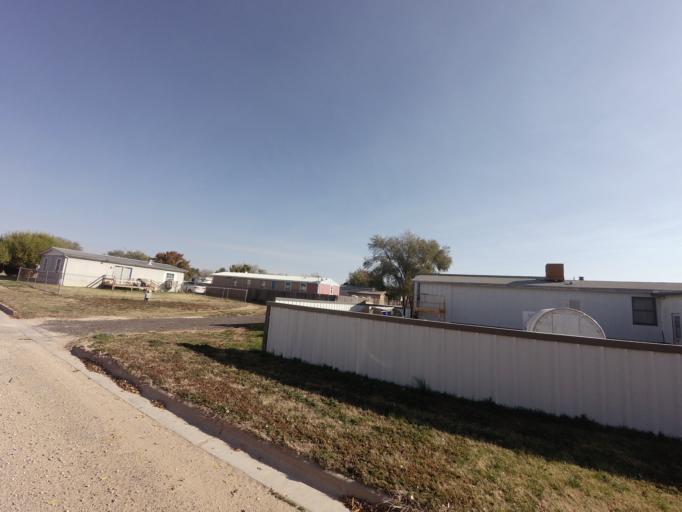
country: US
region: New Mexico
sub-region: Curry County
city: Clovis
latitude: 34.4069
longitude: -103.1751
